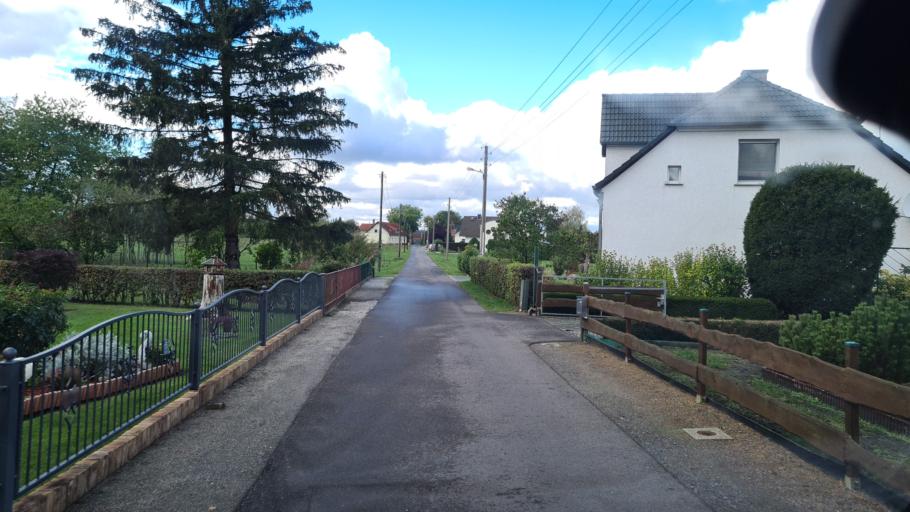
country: DE
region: Brandenburg
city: Grossraschen
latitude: 51.5800
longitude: 13.9595
